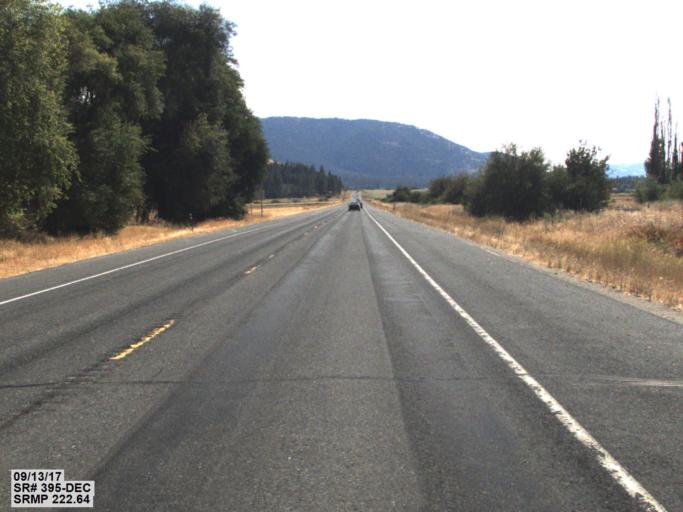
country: US
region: Washington
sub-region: Stevens County
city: Colville
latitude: 48.4509
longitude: -117.8747
